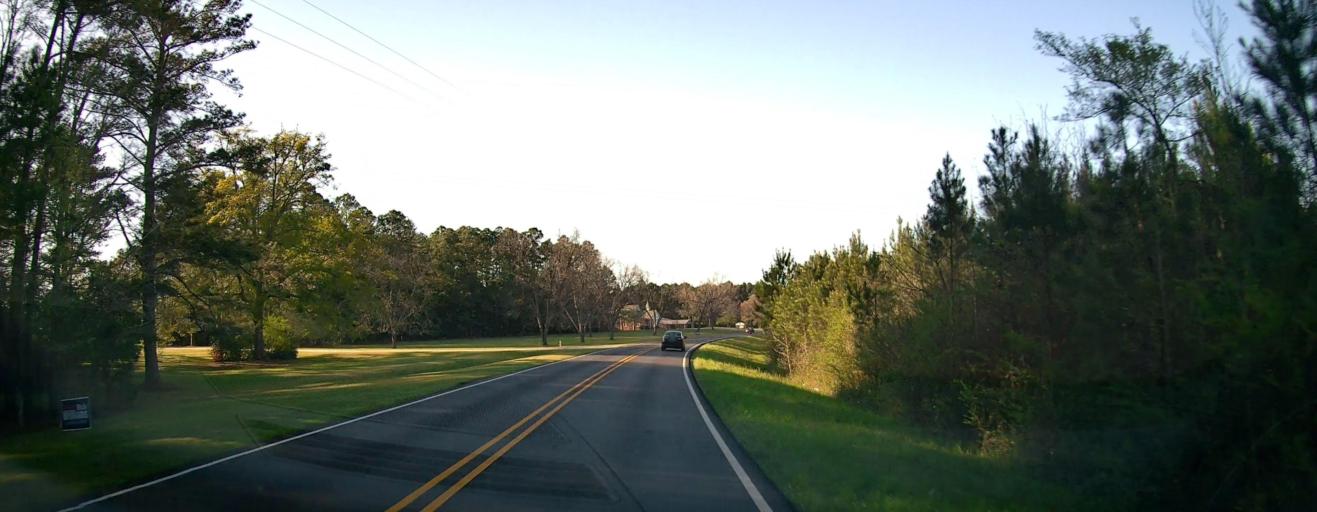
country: US
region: Georgia
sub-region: Butts County
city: Jackson
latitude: 33.3351
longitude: -83.9097
